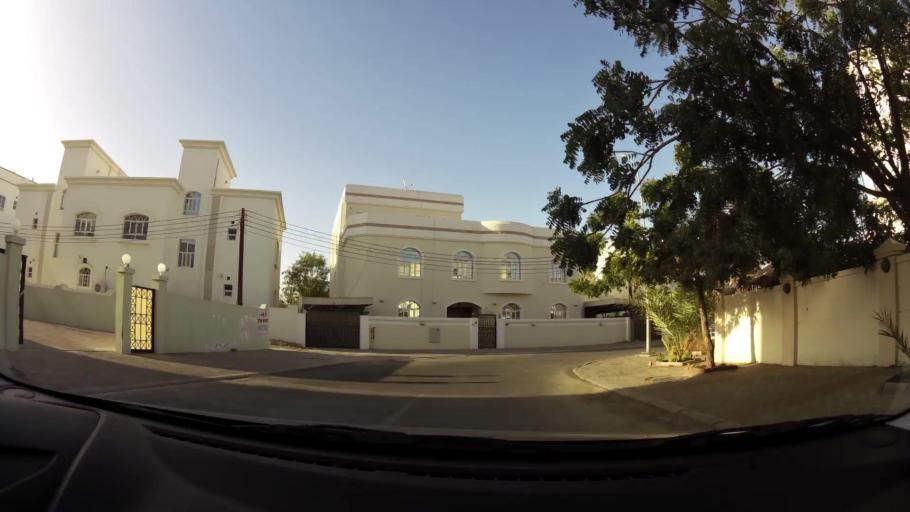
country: OM
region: Muhafazat Masqat
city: As Sib al Jadidah
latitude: 23.6127
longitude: 58.2221
